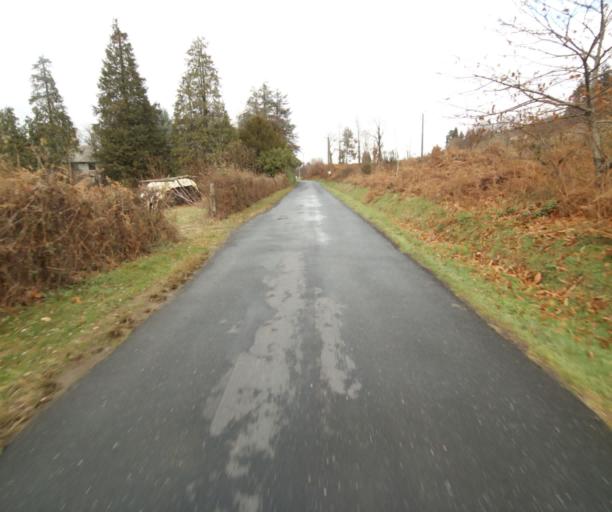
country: FR
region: Limousin
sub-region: Departement de la Correze
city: Saint-Mexant
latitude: 45.2794
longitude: 1.6401
